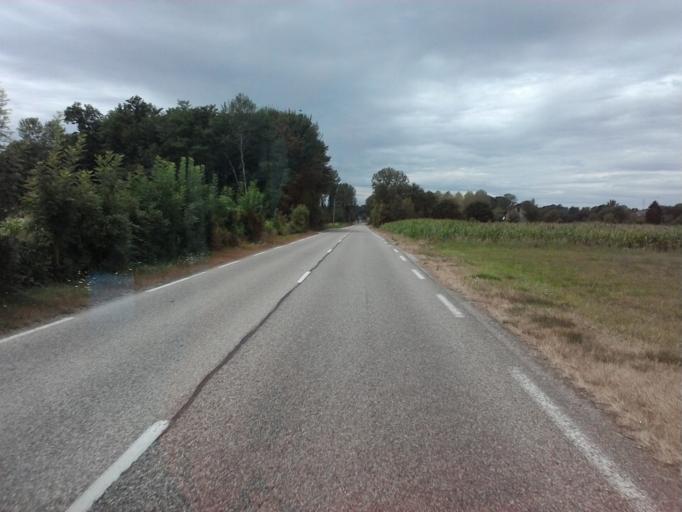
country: FR
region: Rhone-Alpes
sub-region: Departement de l'Isere
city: Corbelin
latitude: 45.5816
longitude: 5.5628
